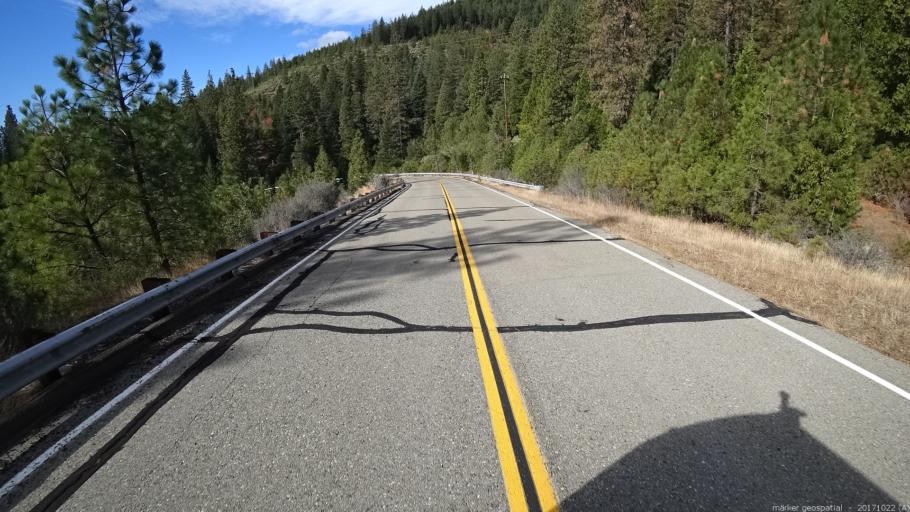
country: US
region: California
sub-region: Siskiyou County
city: Dunsmuir
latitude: 41.0628
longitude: -122.3717
